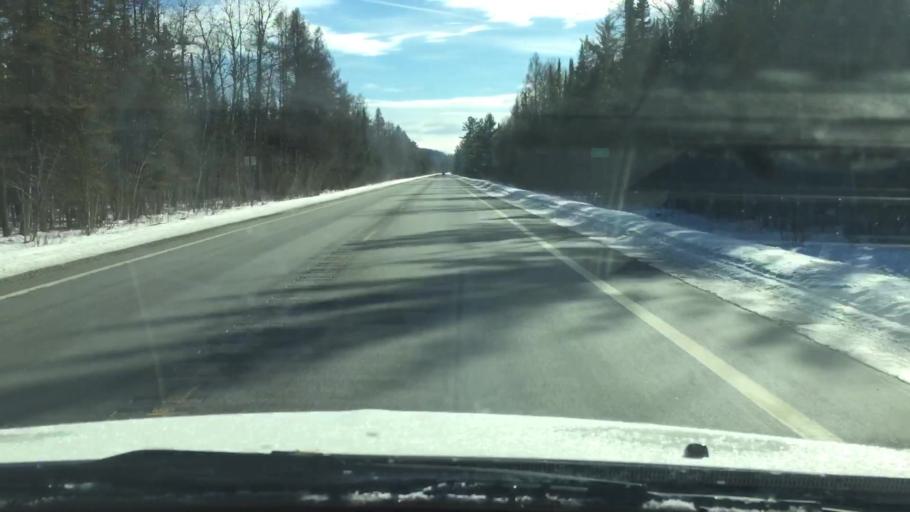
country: US
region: Michigan
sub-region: Antrim County
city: Mancelona
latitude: 45.0289
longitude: -85.0664
